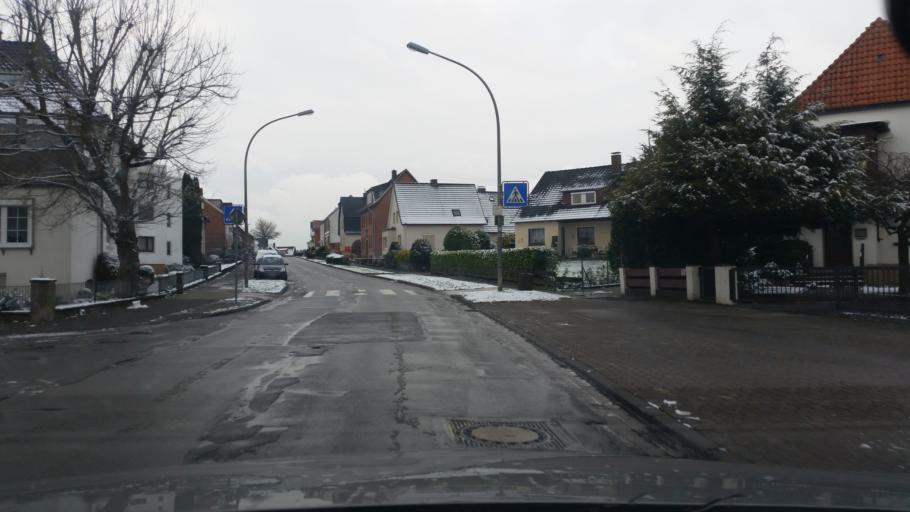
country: DE
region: Lower Saxony
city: Bad Munder am Deister
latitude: 52.1897
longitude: 9.4677
